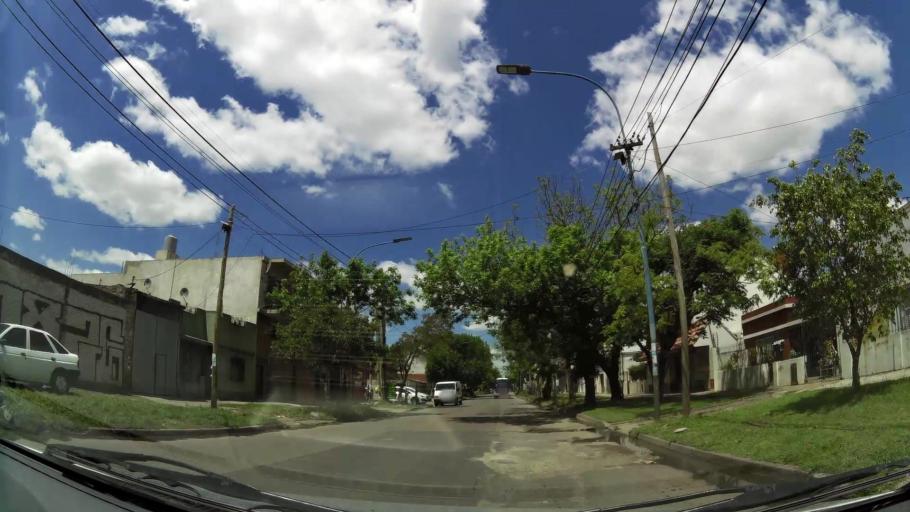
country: AR
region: Buenos Aires
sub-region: Partido de Lanus
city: Lanus
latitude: -34.7165
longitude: -58.4141
